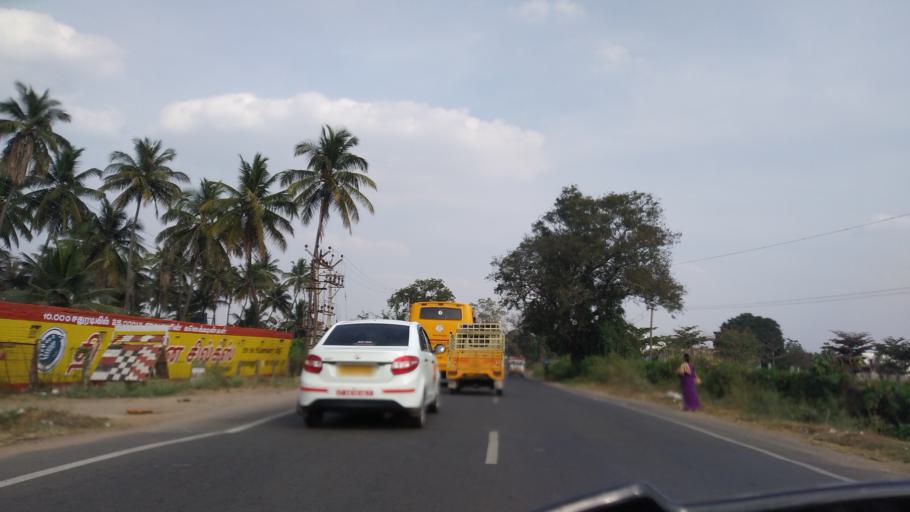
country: IN
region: Tamil Nadu
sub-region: Coimbatore
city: Perur
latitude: 10.9728
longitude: 76.8768
